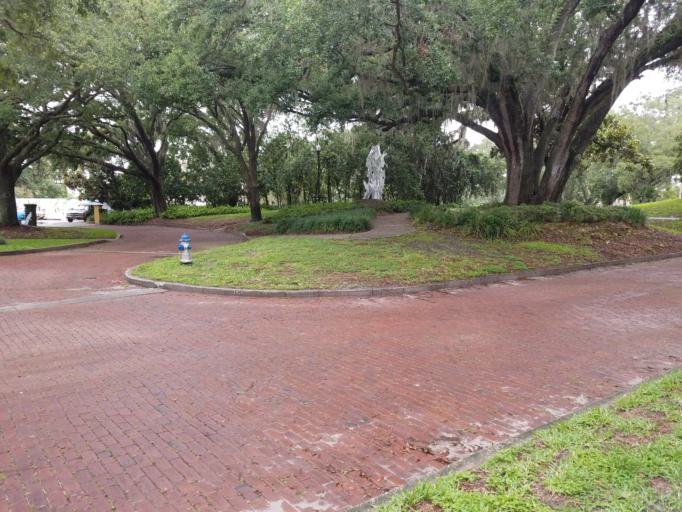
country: US
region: Florida
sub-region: Orange County
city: Fairview Shores
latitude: 28.5704
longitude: -81.3671
